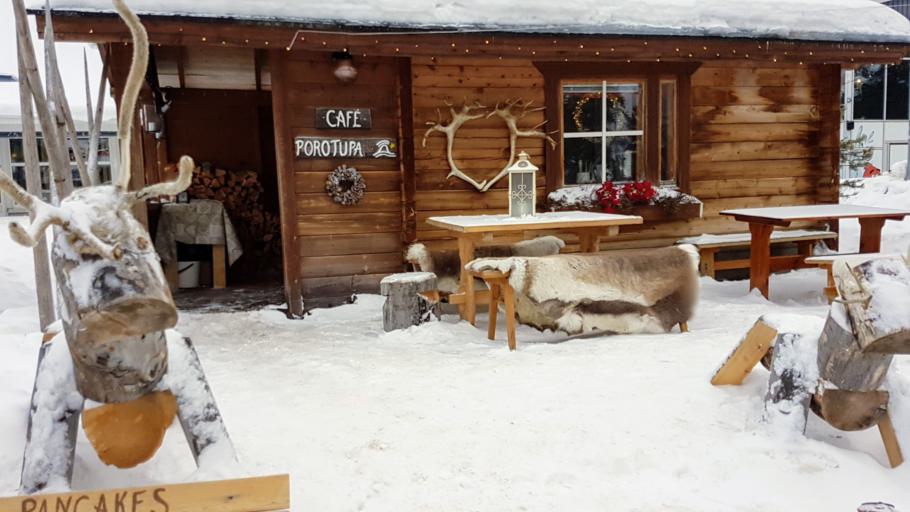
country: FI
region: Lapland
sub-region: Pohjois-Lappi
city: Ivalo
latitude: 68.4200
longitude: 27.4189
